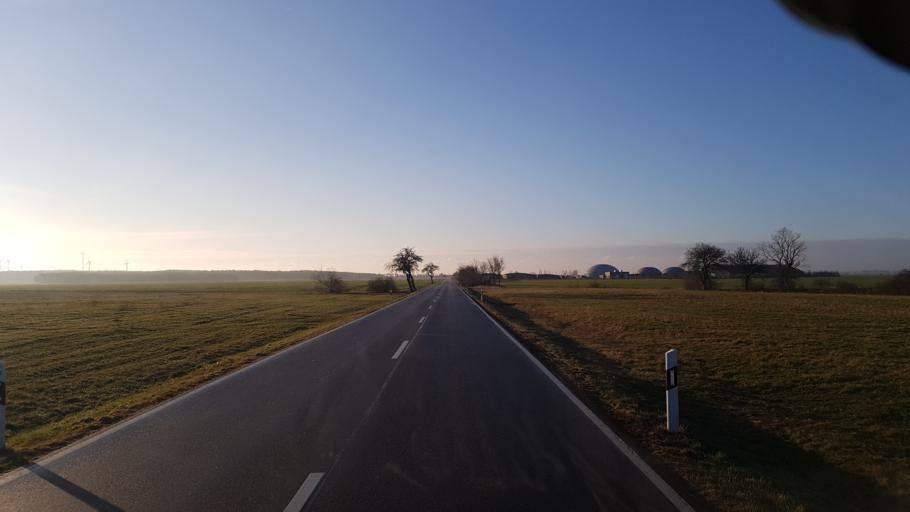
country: DE
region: Saxony
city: Arzberg
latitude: 51.5387
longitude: 13.1714
